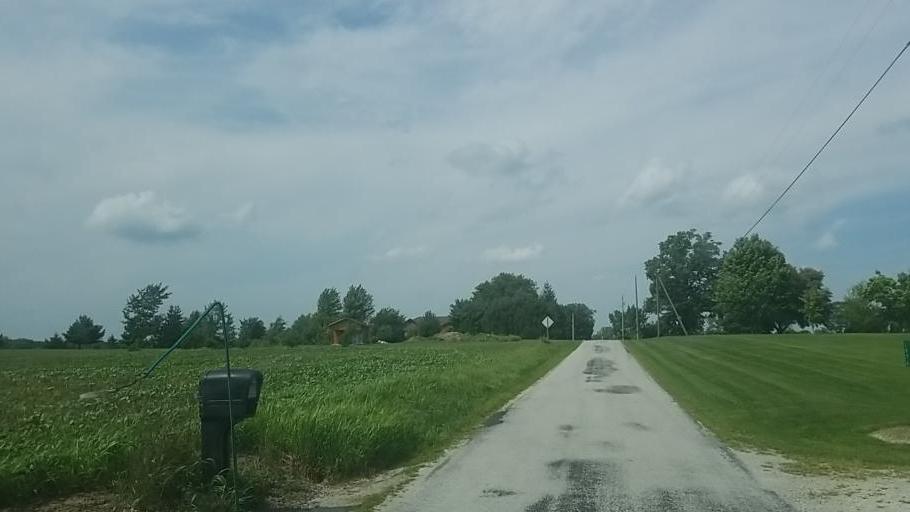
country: US
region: Ohio
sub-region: Hardin County
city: Forest
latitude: 40.7903
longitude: -83.5529
